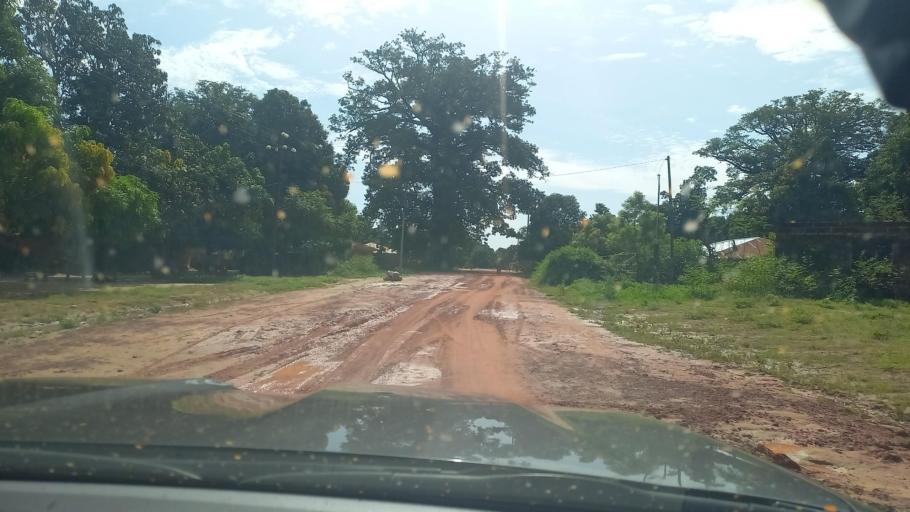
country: SN
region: Ziguinchor
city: Ziguinchor
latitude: 12.6756
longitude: -16.1962
